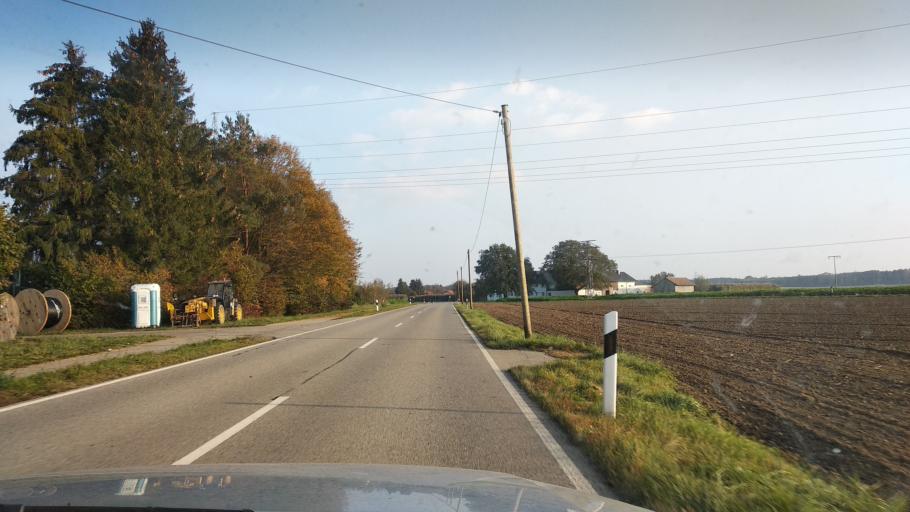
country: DE
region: Bavaria
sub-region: Upper Bavaria
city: Worth
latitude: 48.2431
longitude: 11.9103
